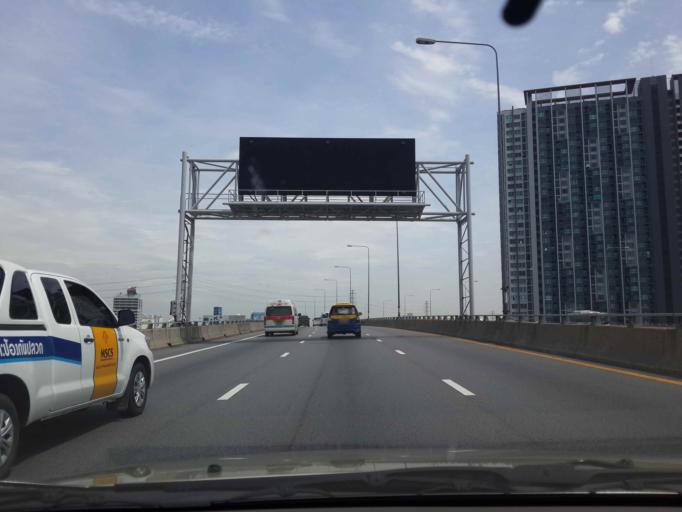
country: TH
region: Bangkok
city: Watthana
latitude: 13.7466
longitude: 100.6068
